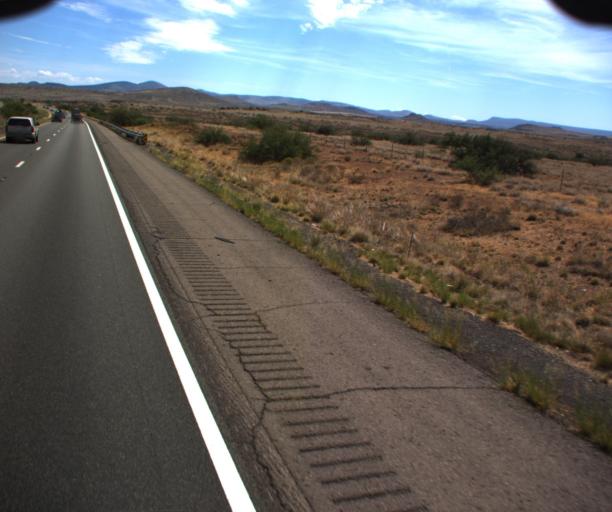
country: US
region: Arizona
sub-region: Yavapai County
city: Cordes Lakes
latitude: 34.3843
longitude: -112.0919
